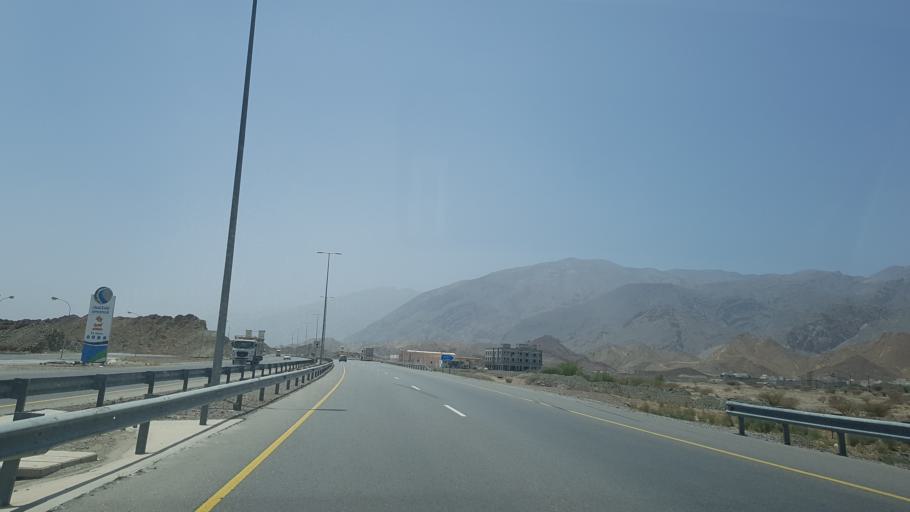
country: OM
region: Muhafazat ad Dakhiliyah
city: Sufalat Sama'il
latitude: 23.3224
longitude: 57.9615
